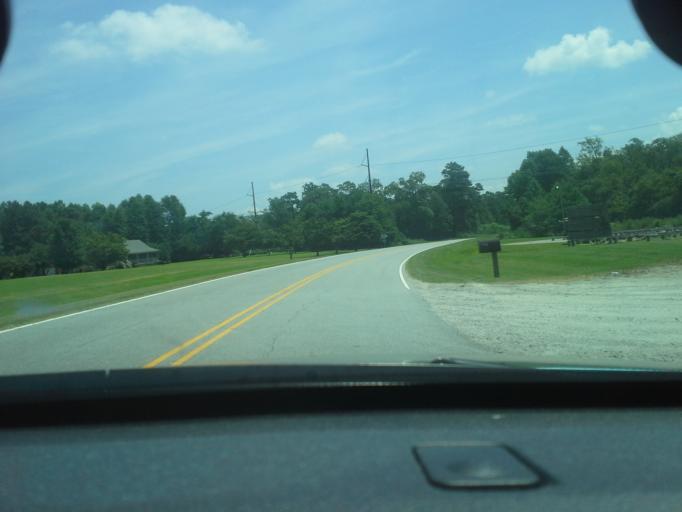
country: US
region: North Carolina
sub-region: Chowan County
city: Edenton
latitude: 35.9309
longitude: -76.6151
